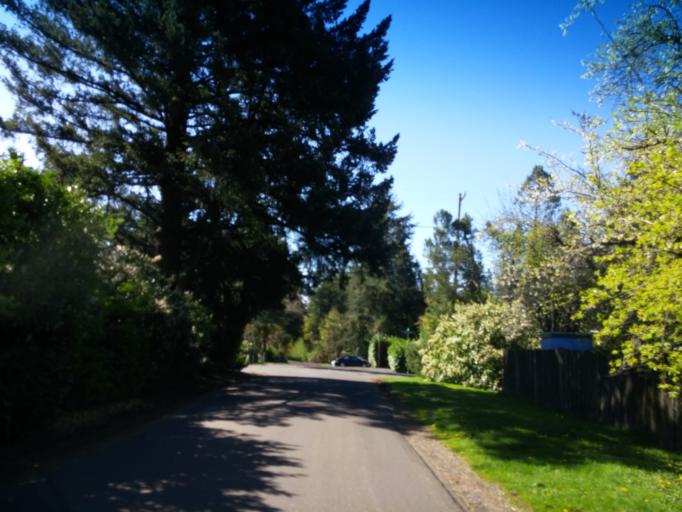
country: US
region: Oregon
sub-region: Washington County
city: West Haven
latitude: 45.5177
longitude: -122.7748
